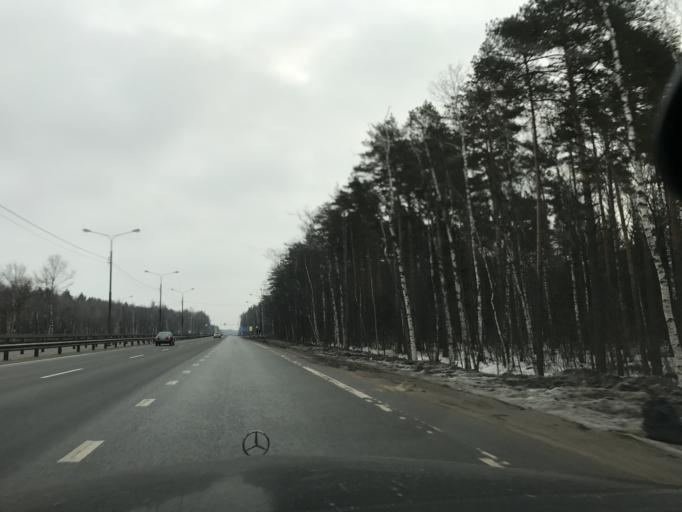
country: RU
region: Moskovskaya
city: Malaya Dubna
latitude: 55.8613
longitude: 38.8989
